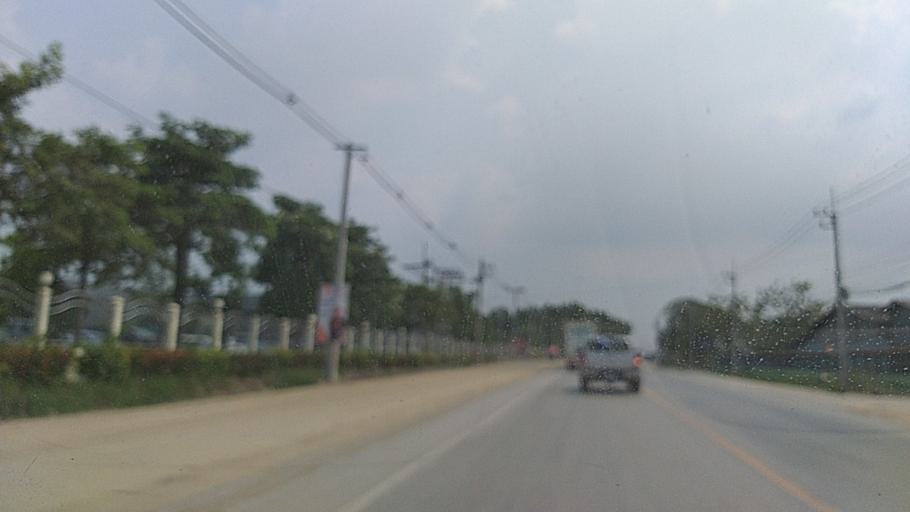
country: TH
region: Chon Buri
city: Phanat Nikhom
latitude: 13.3616
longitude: 101.1966
